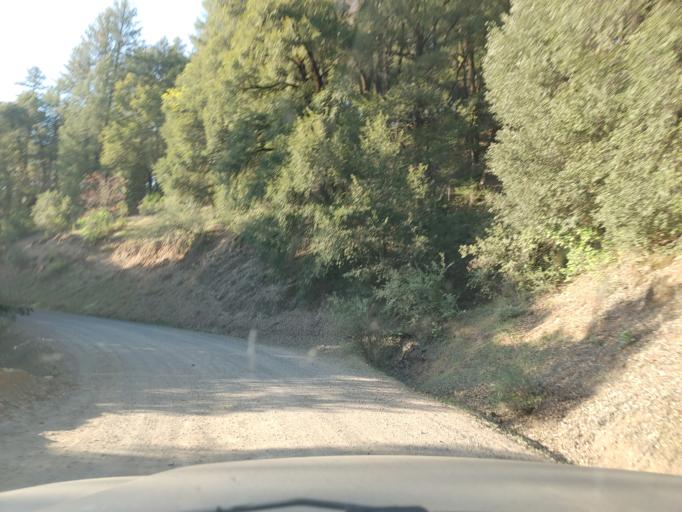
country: US
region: California
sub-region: Shasta County
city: Bella Vista
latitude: 40.8160
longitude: -122.0060
